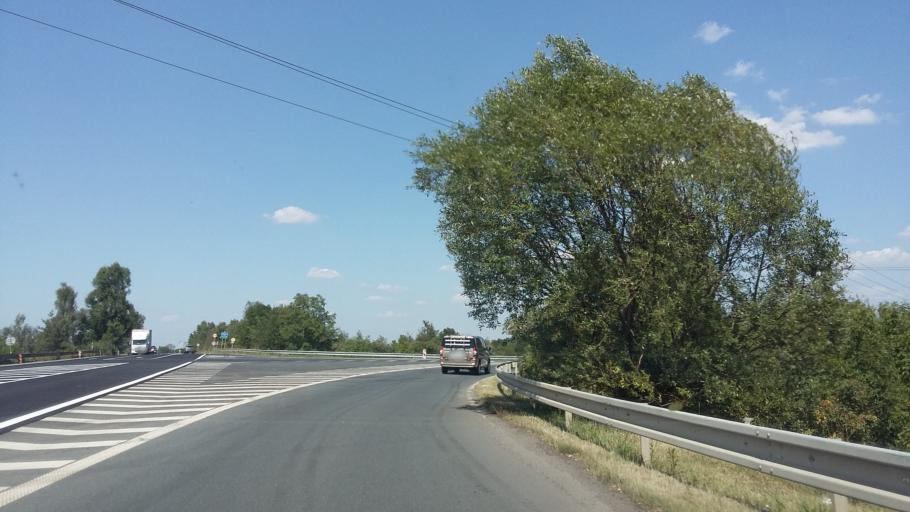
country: CZ
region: Central Bohemia
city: Brandys nad Labem-Stara Boleslav
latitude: 50.1680
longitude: 14.6748
